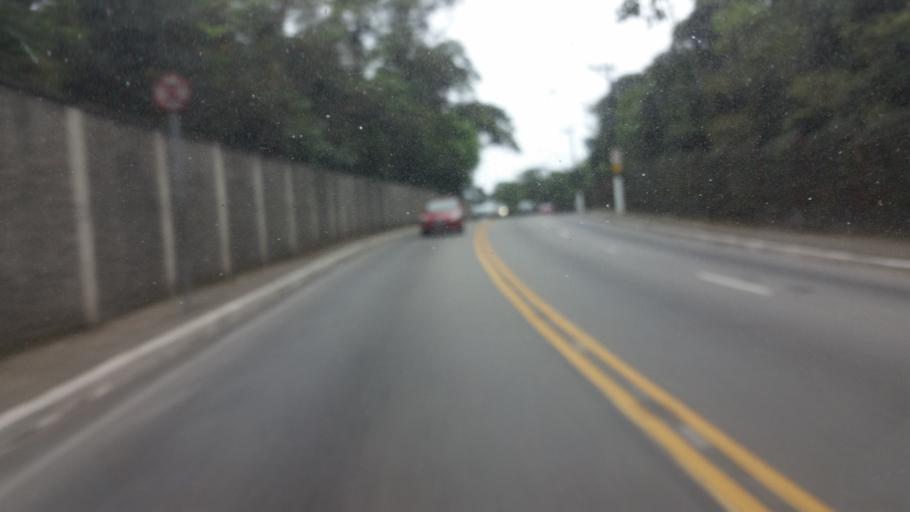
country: BR
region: Sao Paulo
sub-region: Diadema
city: Diadema
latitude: -23.6549
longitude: -46.6169
